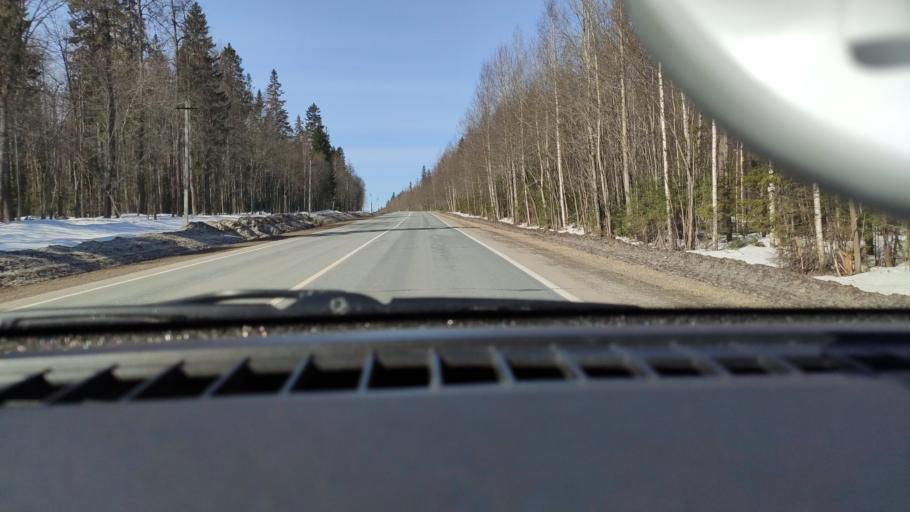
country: RU
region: Perm
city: Perm
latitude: 58.2081
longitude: 56.1937
